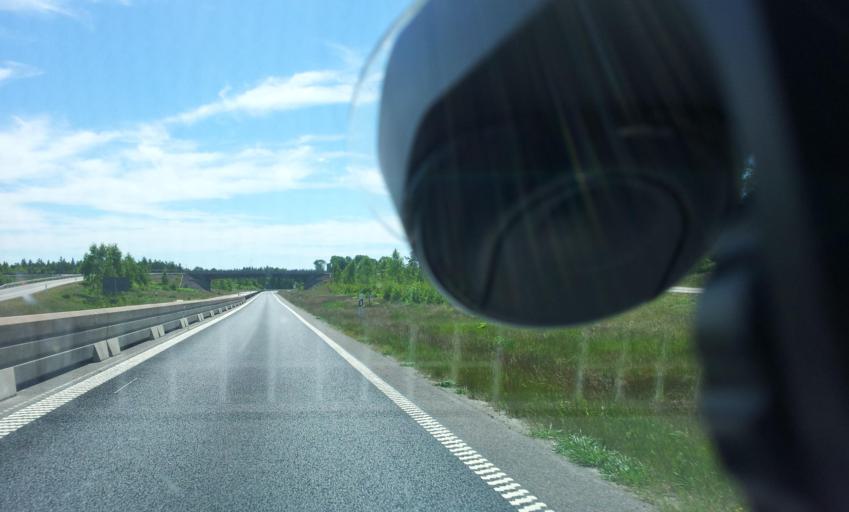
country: SE
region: Kalmar
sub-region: Oskarshamns Kommun
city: Oskarshamn
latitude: 57.3752
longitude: 16.4874
